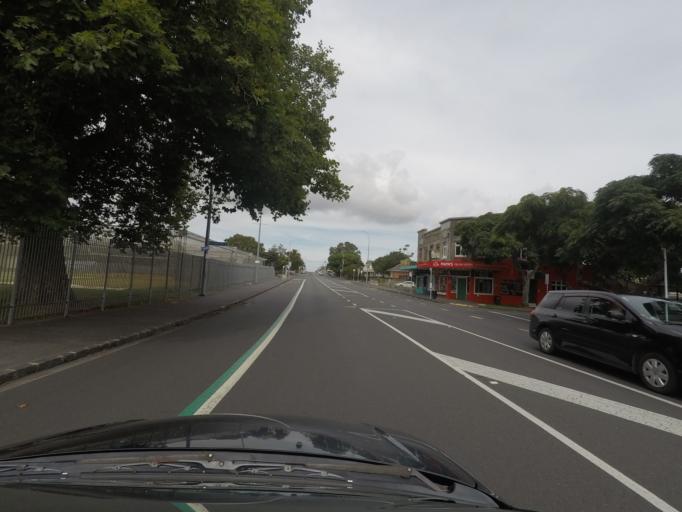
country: NZ
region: Auckland
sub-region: Auckland
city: Auckland
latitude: -36.8745
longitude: 174.7419
